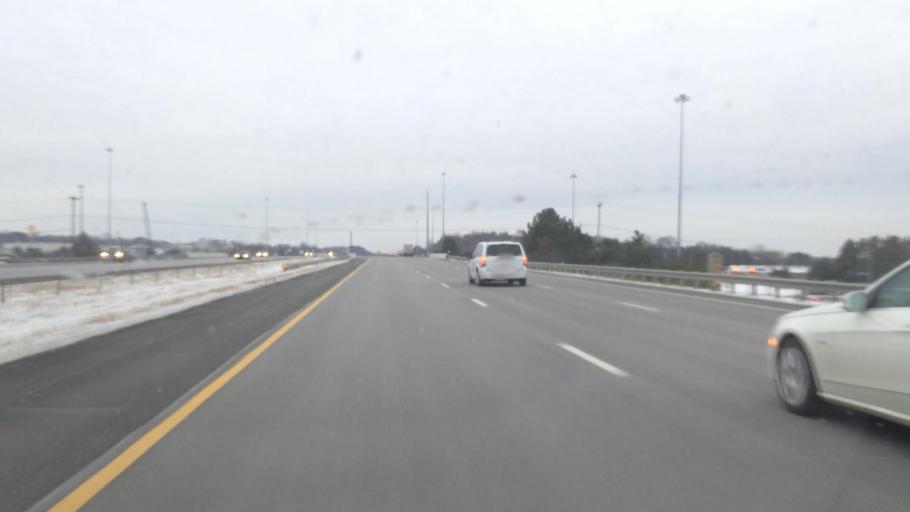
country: US
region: Ohio
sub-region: Medina County
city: Brunswick
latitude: 41.2401
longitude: -81.7990
